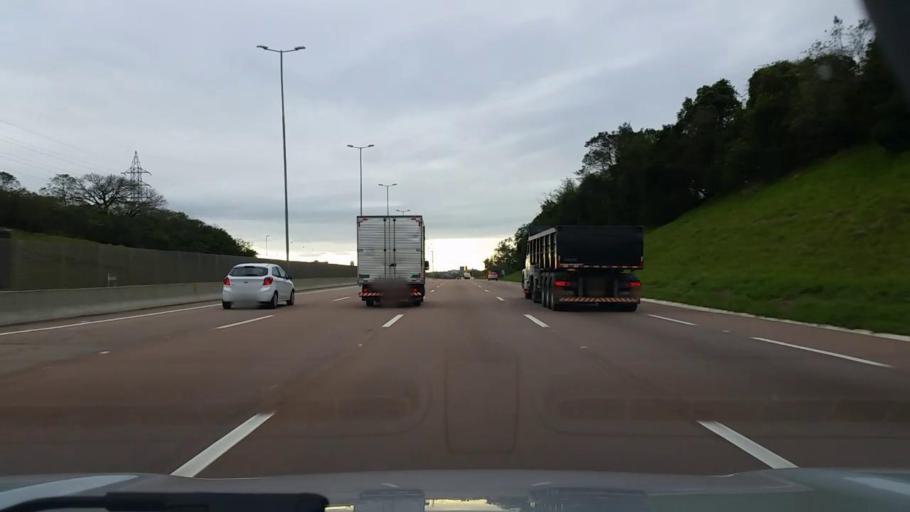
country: BR
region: Rio Grande do Sul
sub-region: Gravatai
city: Gravatai
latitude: -29.9557
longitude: -51.0082
